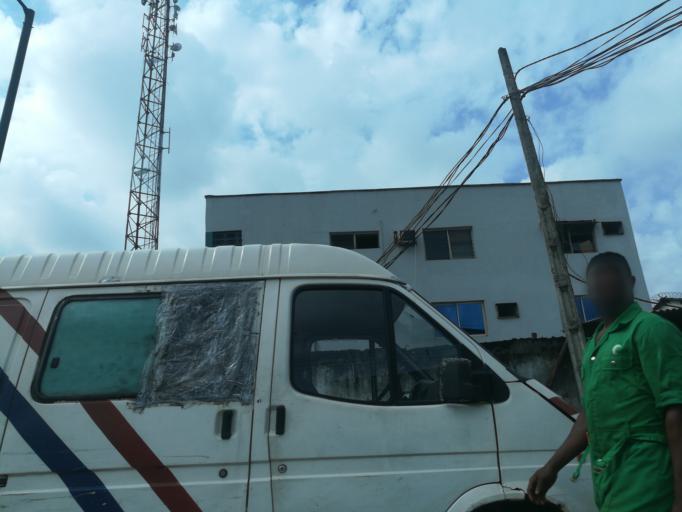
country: NG
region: Lagos
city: Somolu
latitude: 6.5602
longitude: 3.3635
